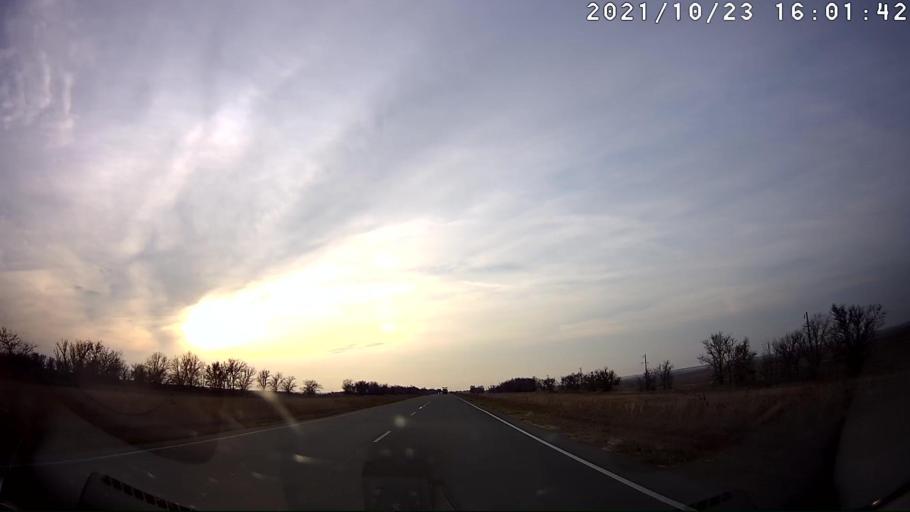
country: RU
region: Kalmykiya
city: Sadovoye
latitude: 47.9286
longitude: 43.8446
